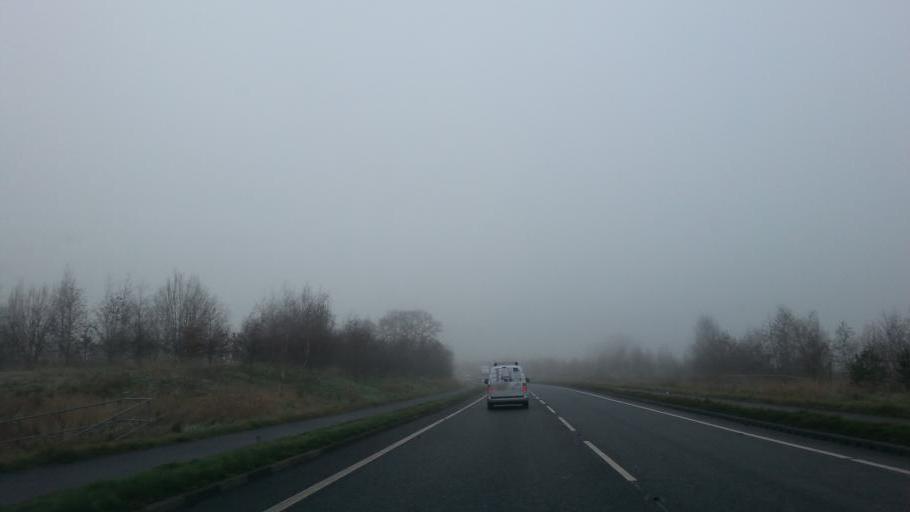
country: GB
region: England
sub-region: Cheshire East
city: Alderley Edge
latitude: 53.2949
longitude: -2.2538
